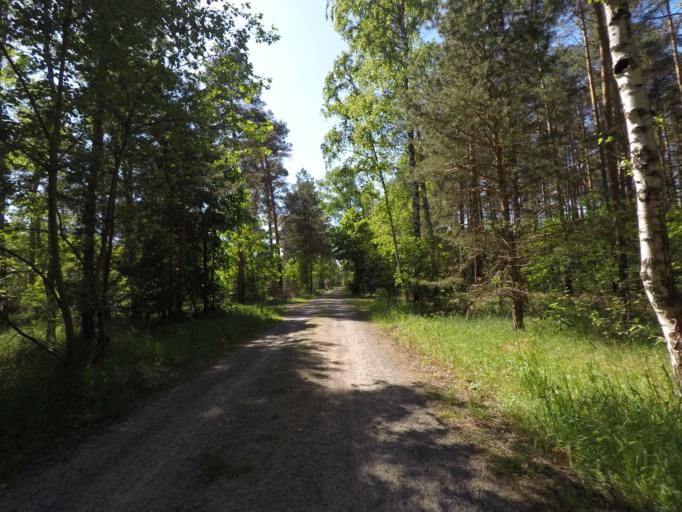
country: DE
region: Brandenburg
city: Melchow
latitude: 52.8275
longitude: 13.7375
